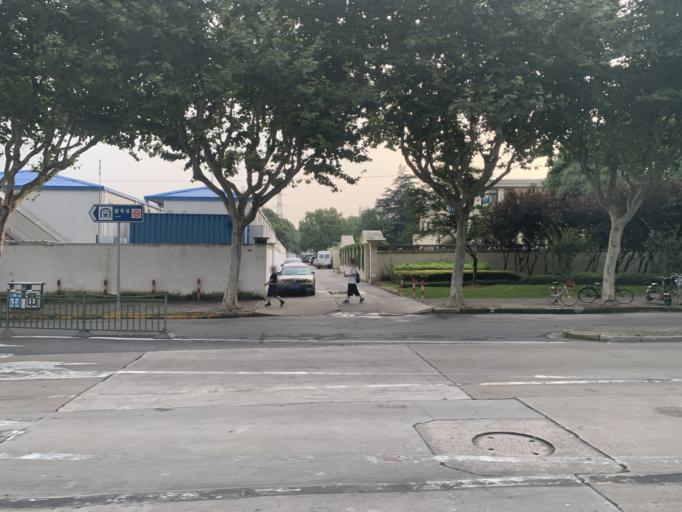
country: CN
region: Shanghai Shi
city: Huamu
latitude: 31.2447
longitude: 121.5726
